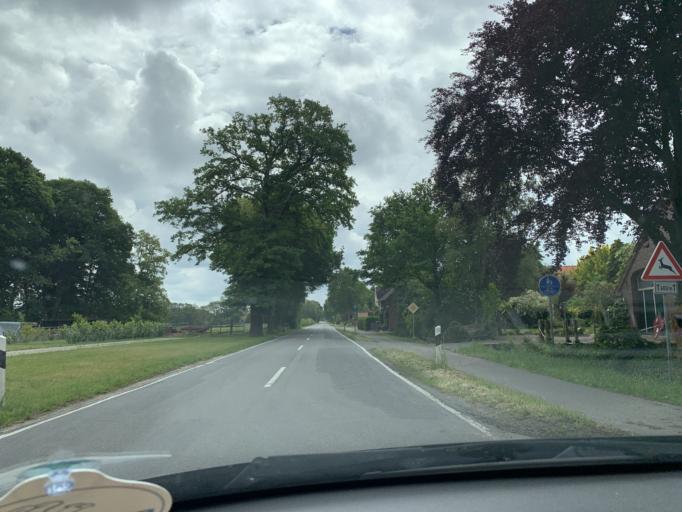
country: DE
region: Lower Saxony
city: Bockhorn
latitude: 53.3670
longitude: 8.0624
